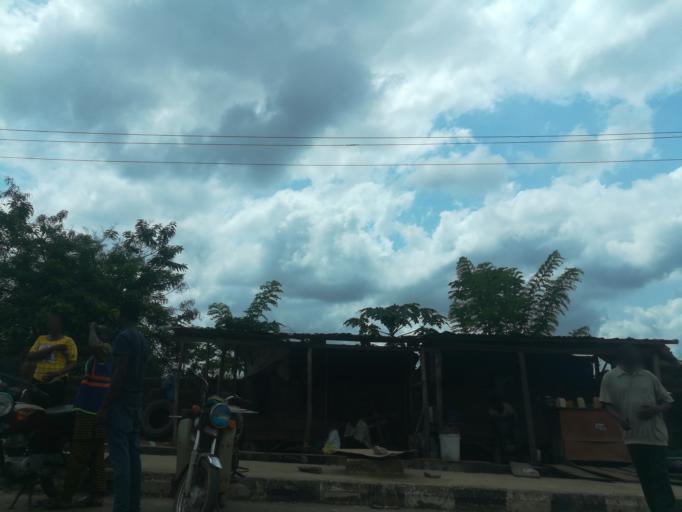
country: NG
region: Oyo
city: Ibadan
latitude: 7.3668
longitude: 3.8284
